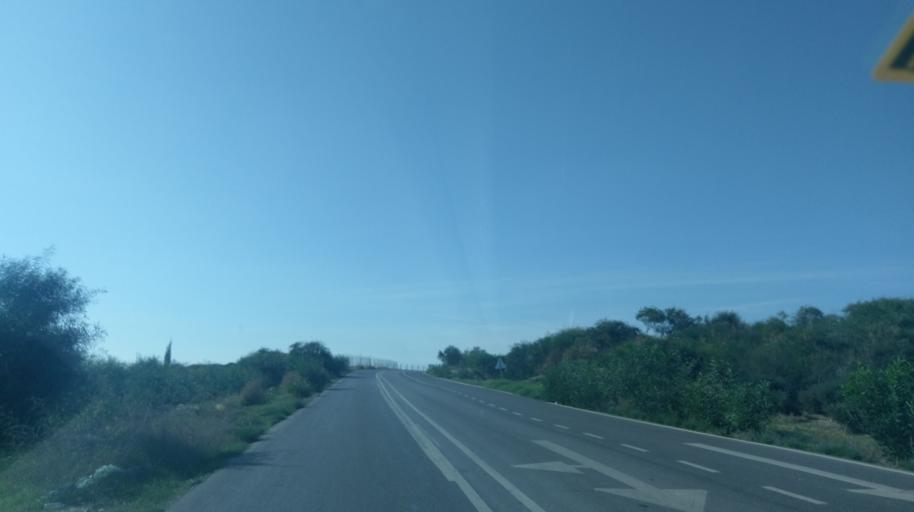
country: CY
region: Larnaka
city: Athienou
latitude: 35.1539
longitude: 33.5178
